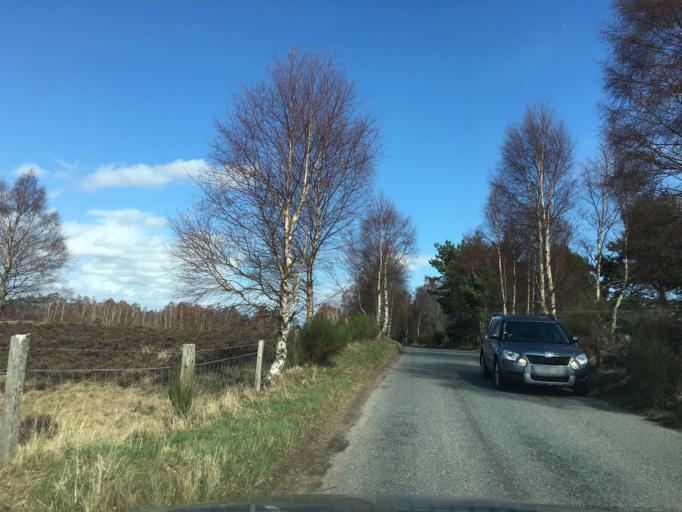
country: GB
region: Scotland
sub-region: Highland
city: Aviemore
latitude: 57.2019
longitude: -3.7964
